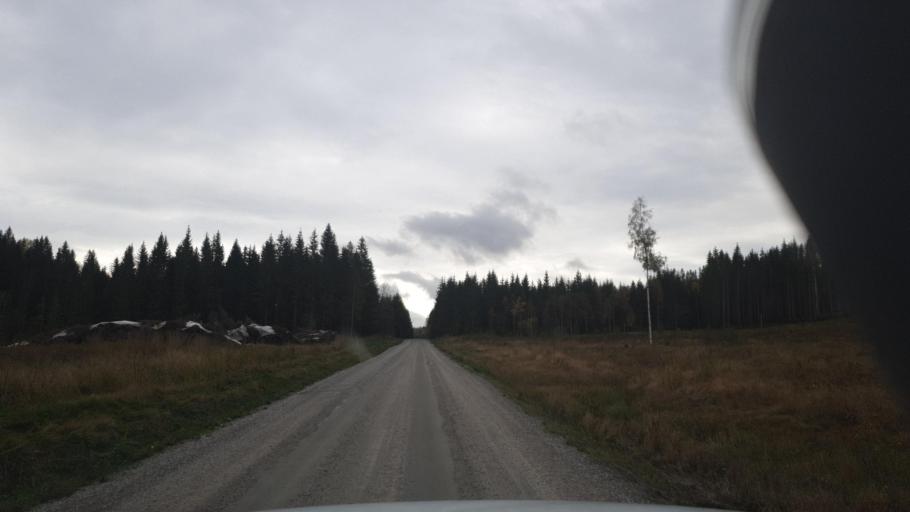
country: SE
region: Vaermland
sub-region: Arvika Kommun
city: Arvika
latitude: 59.8012
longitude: 12.7494
